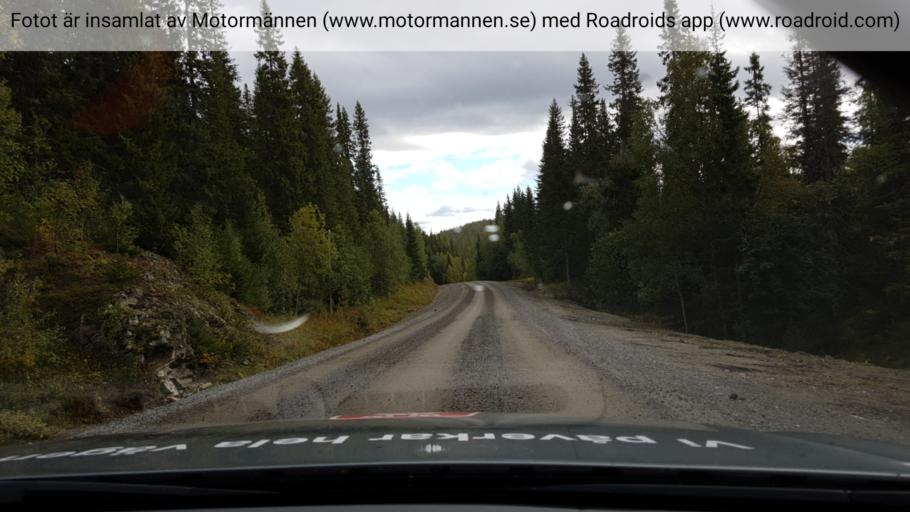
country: NO
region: Nord-Trondelag
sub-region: Snasa
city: Snaase
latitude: 63.7290
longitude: 12.5730
